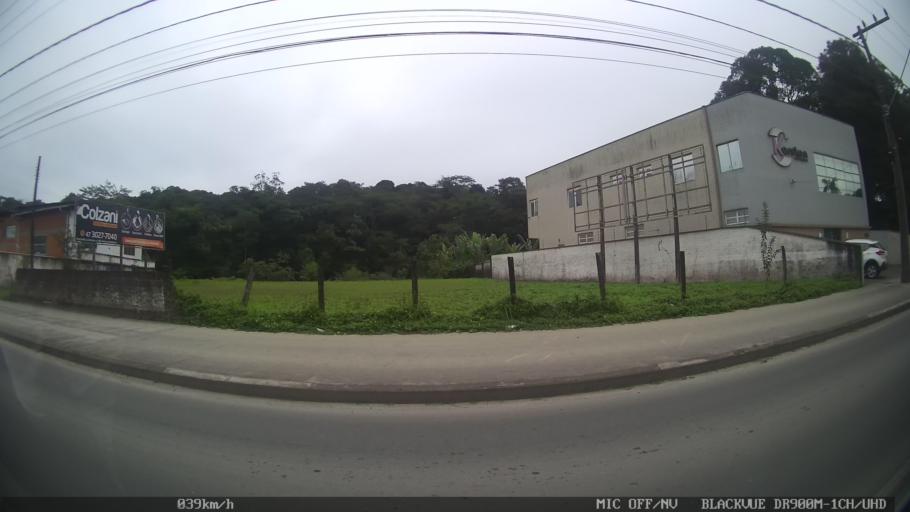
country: BR
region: Santa Catarina
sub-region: Joinville
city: Joinville
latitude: -26.2615
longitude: -48.8514
